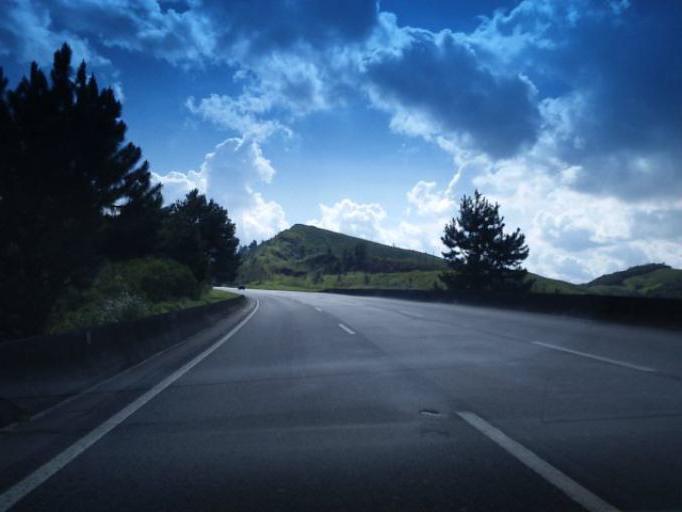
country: BR
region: Parana
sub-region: Campina Grande Do Sul
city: Campina Grande do Sul
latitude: -25.1020
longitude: -48.8320
